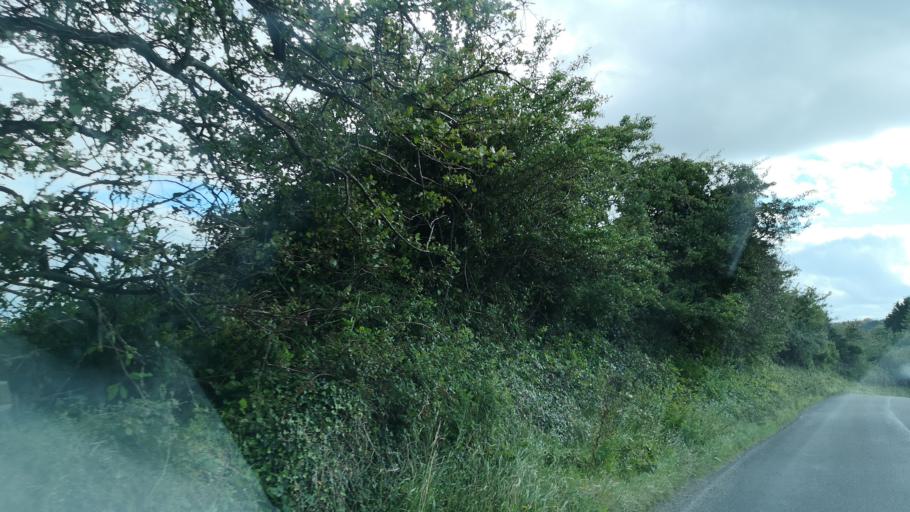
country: IE
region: Connaught
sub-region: County Galway
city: Moycullen
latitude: 53.3459
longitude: -9.1722
